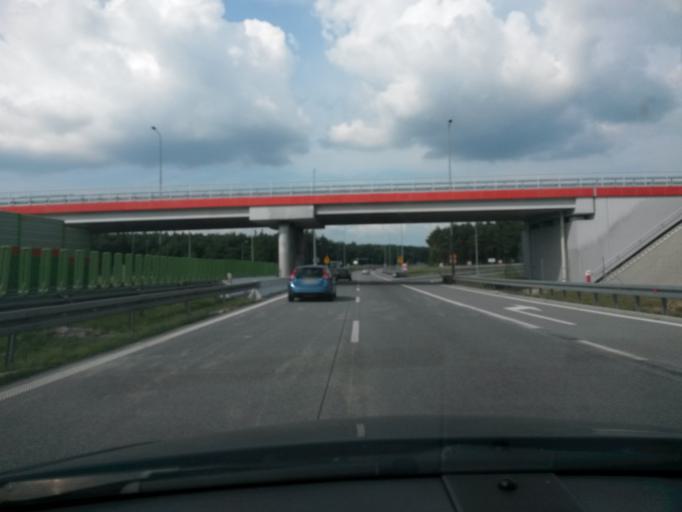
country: PL
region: Lodz Voivodeship
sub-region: Powiat tomaszowski
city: Lubochnia
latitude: 51.6234
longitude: 20.0954
